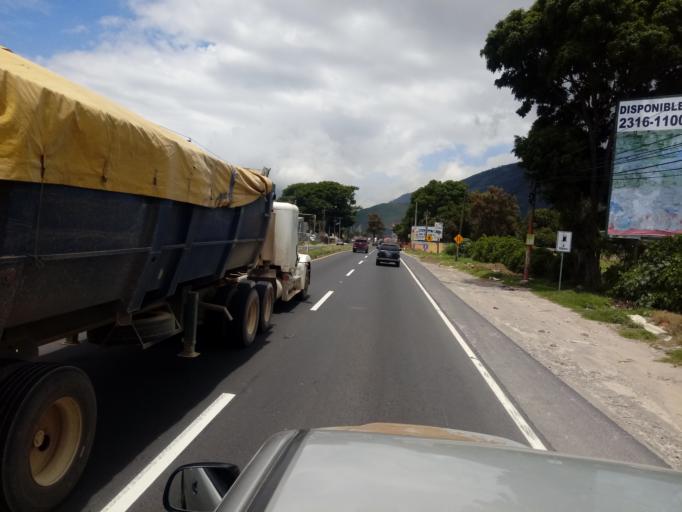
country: GT
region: Guatemala
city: Amatitlan
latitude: 14.4748
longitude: -90.6340
